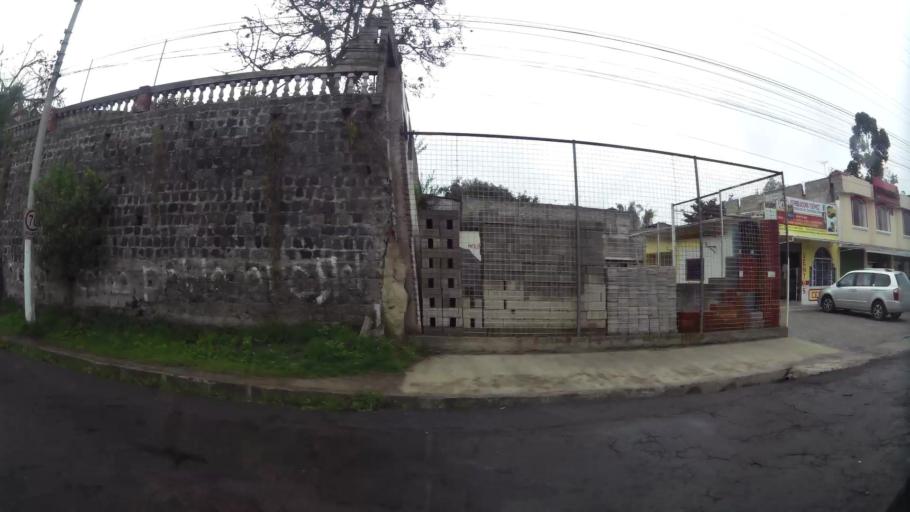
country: EC
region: Pichincha
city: Sangolqui
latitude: -0.2892
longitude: -78.4444
